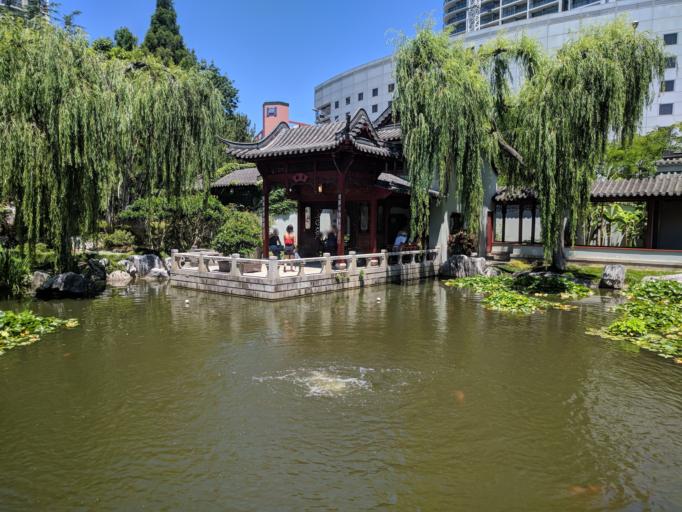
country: AU
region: New South Wales
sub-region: City of Sydney
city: Haymarket
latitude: -33.8767
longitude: 151.2027
